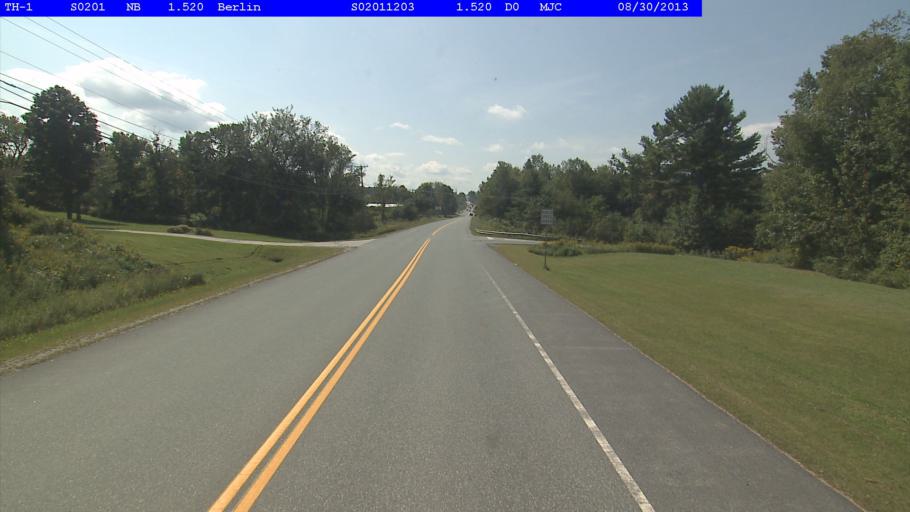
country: US
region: Vermont
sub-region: Washington County
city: Montpelier
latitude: 44.2182
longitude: -72.5721
